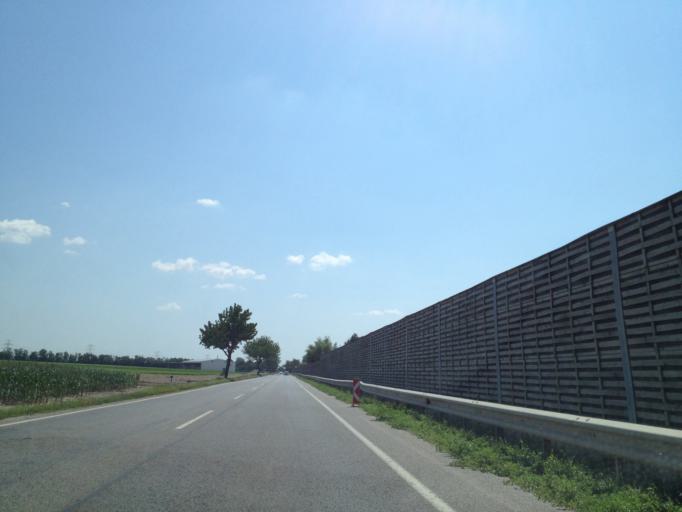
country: AT
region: Lower Austria
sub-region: Politischer Bezirk Ganserndorf
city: Gross-Enzersdorf
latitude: 48.1874
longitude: 16.5832
